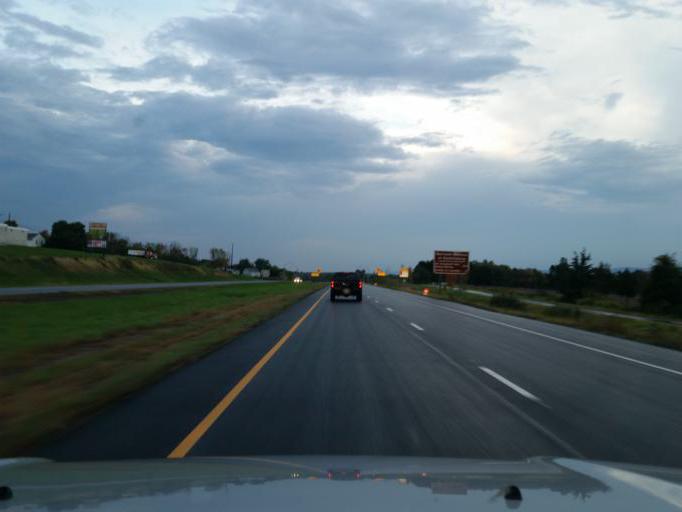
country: US
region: Maryland
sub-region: Frederick County
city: Emmitsburg
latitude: 39.7176
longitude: -77.3082
